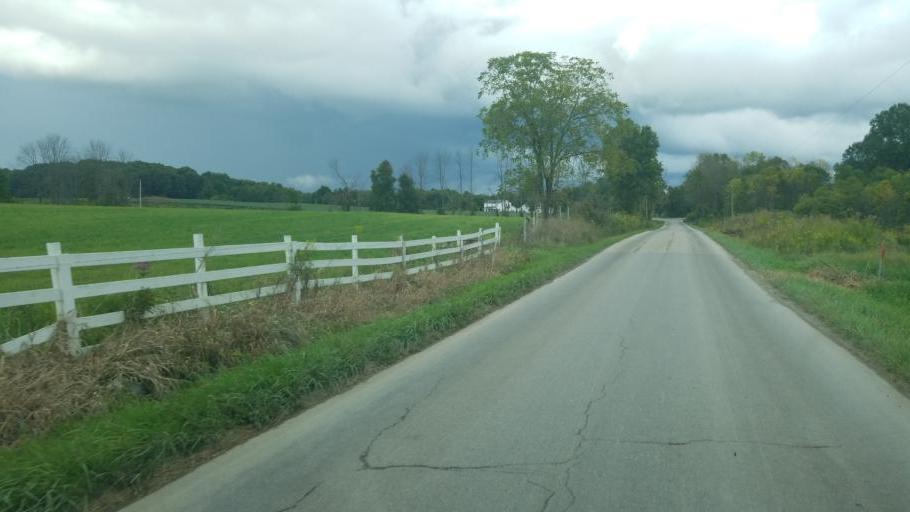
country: US
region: Ohio
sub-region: Jackson County
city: Oak Hill
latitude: 38.9468
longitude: -82.6238
